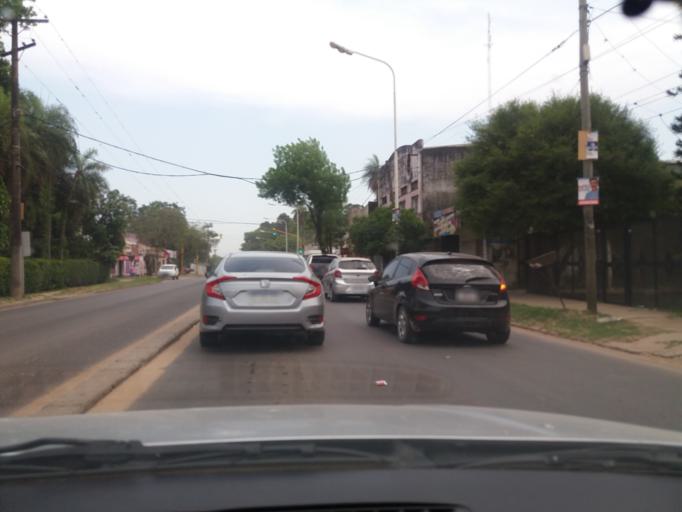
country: AR
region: Corrientes
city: Corrientes
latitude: -27.5027
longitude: -58.8125
